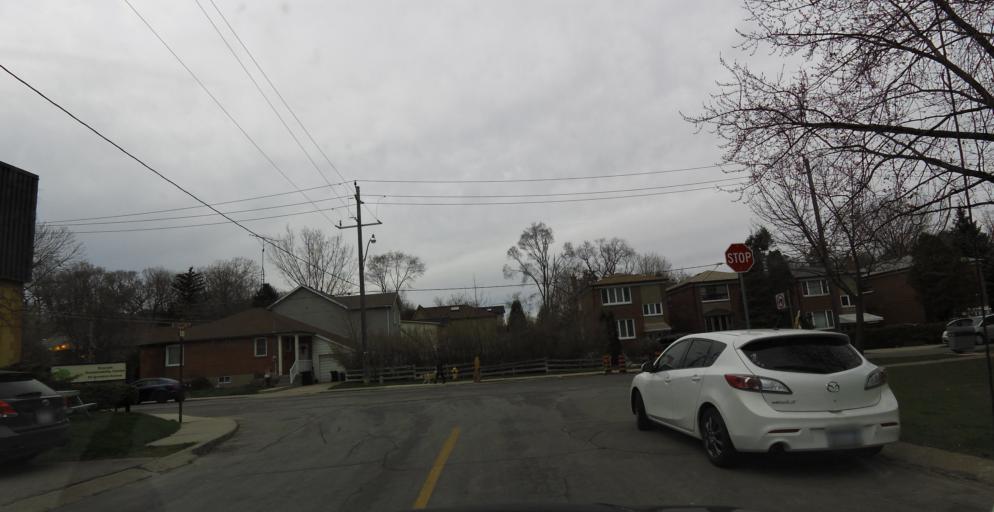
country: CA
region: Ontario
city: Toronto
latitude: 43.6389
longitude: -79.4760
